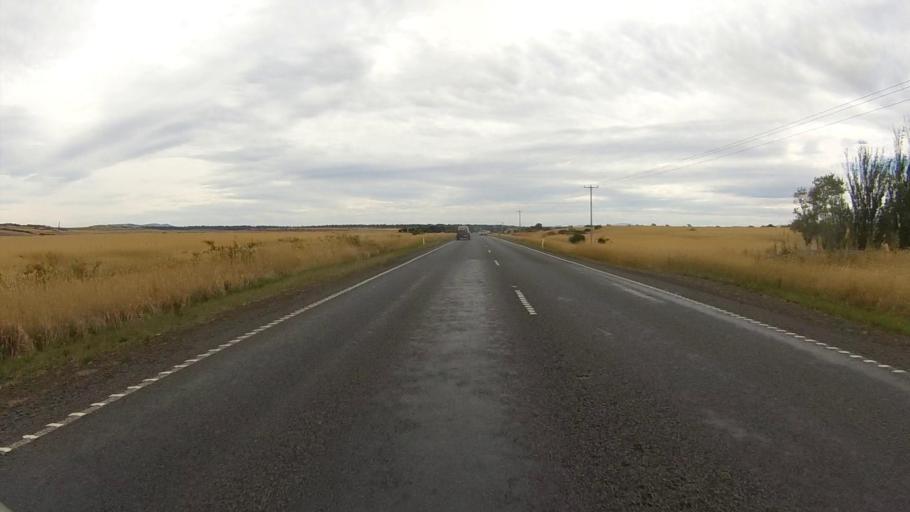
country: AU
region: Tasmania
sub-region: Northern Midlands
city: Evandale
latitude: -41.8609
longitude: 147.4557
